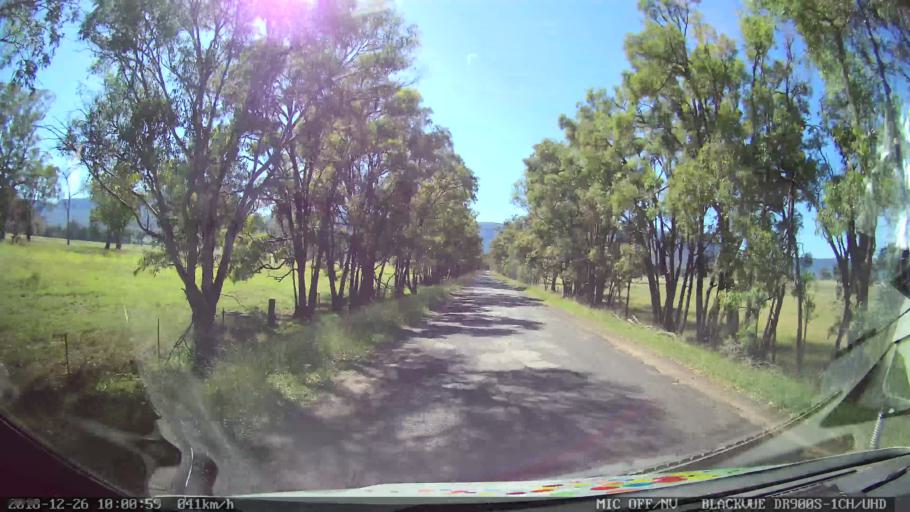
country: AU
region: New South Wales
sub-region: Mid-Western Regional
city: Kandos
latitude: -33.0456
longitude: 150.2190
